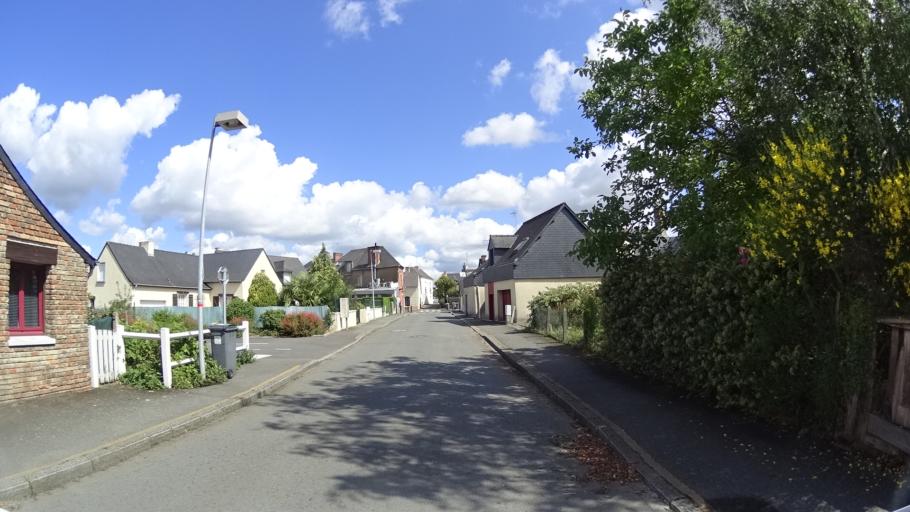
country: FR
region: Brittany
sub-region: Departement d'Ille-et-Vilaine
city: Chartres-de-Bretagne
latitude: 48.0410
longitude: -1.7031
